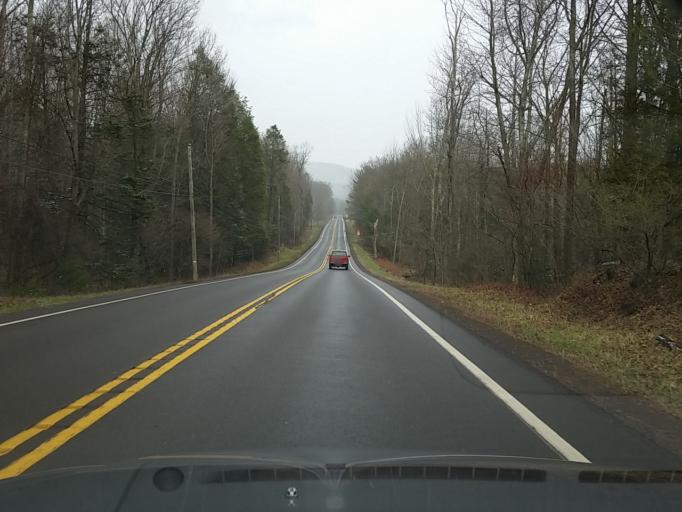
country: US
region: Pennsylvania
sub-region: Luzerne County
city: East Berwick
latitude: 41.2932
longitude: -76.2913
